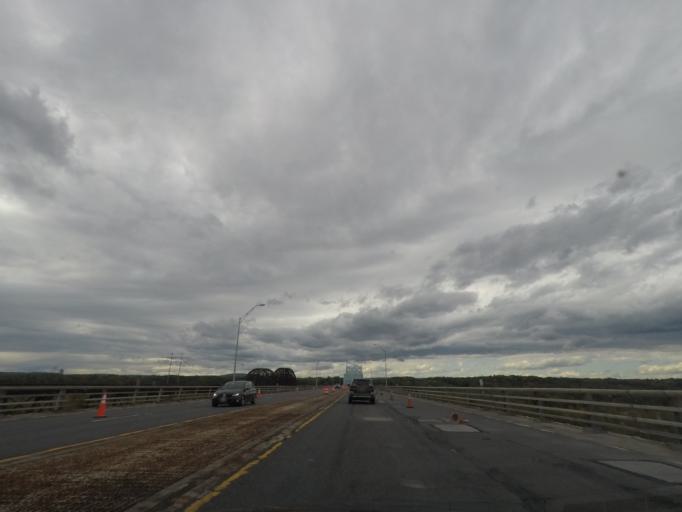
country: US
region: New York
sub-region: Rensselaer County
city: Castleton-on-Hudson
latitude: 42.5075
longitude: -73.7670
